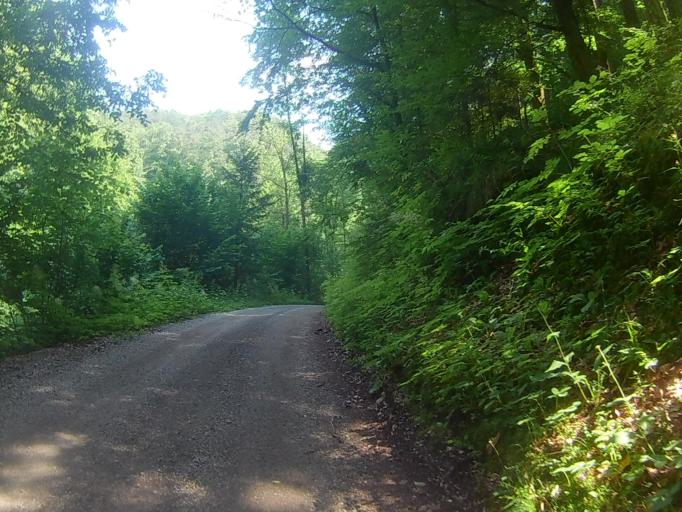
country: SI
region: Maribor
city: Bresternica
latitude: 46.5804
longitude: 15.5831
